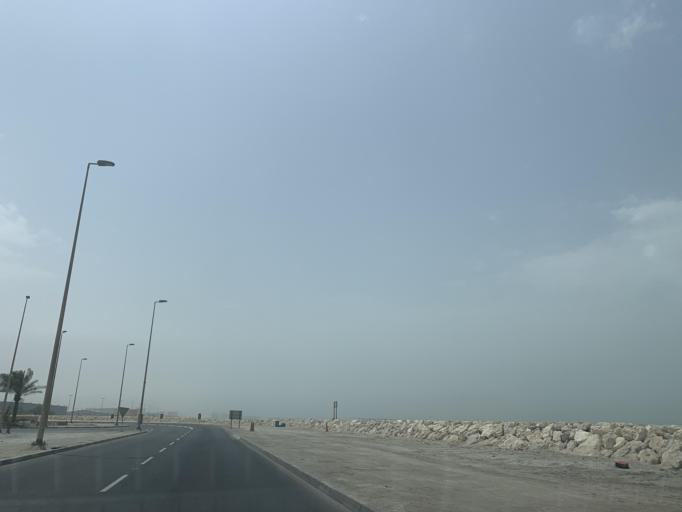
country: BH
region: Muharraq
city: Al Hadd
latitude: 26.2260
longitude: 50.6984
